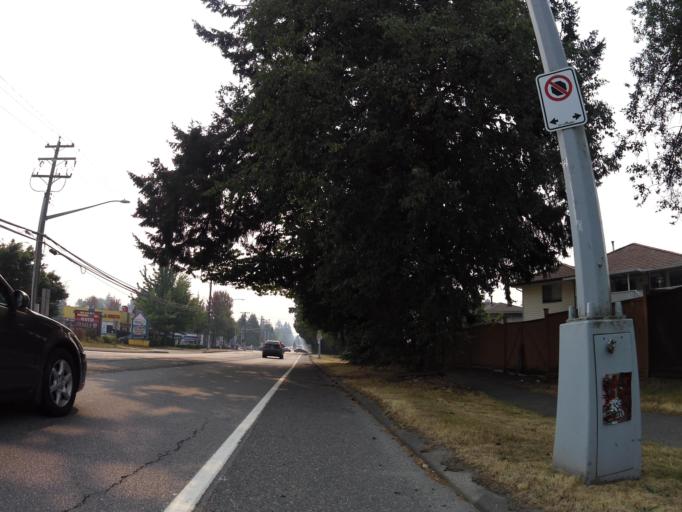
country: CA
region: British Columbia
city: Surrey
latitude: 49.1352
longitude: -122.8567
